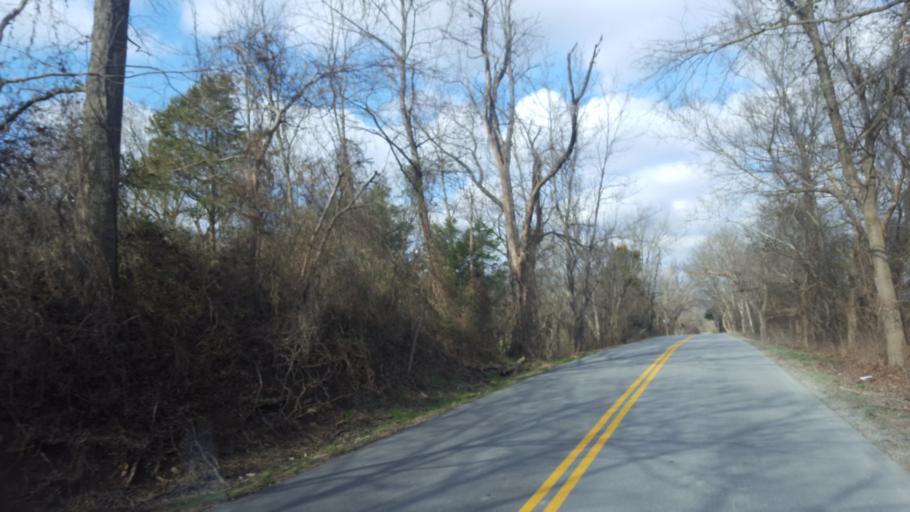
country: US
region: Kentucky
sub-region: Owen County
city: Owenton
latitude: 38.4594
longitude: -84.9589
